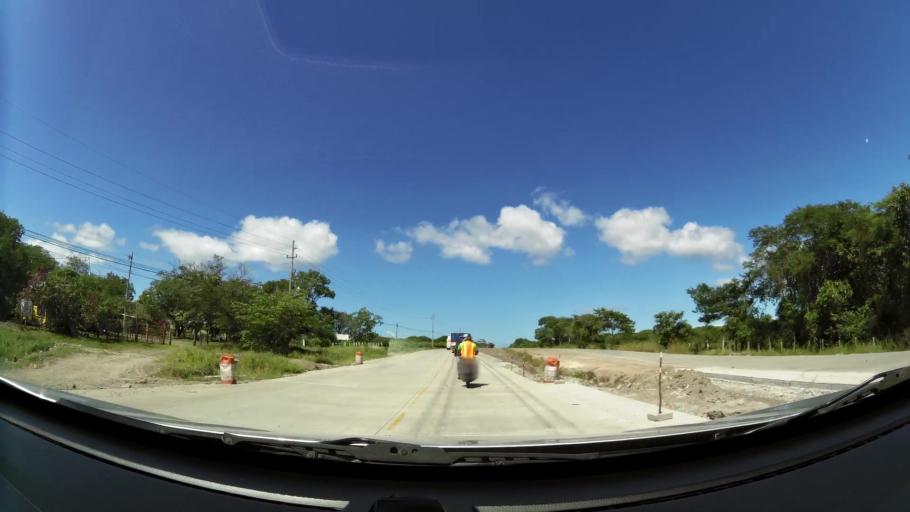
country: CR
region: Guanacaste
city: Bagaces
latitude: 10.5029
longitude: -85.2311
